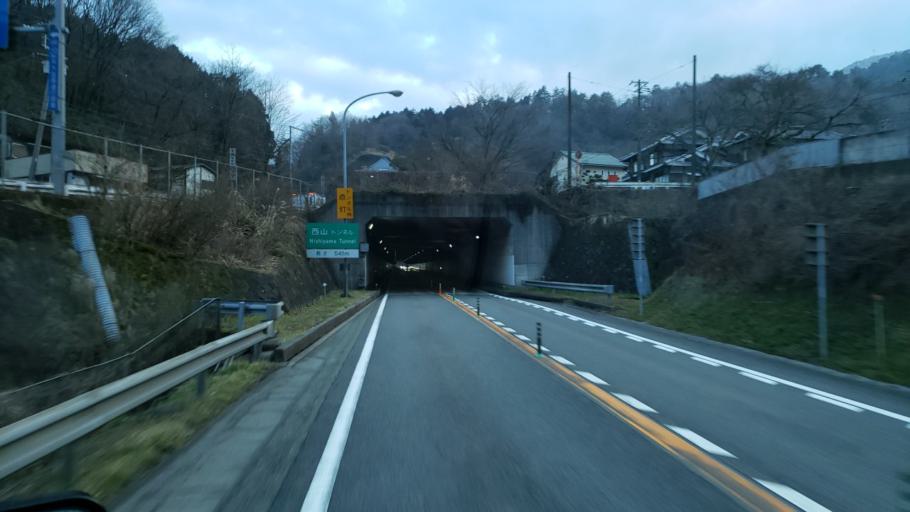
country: JP
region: Hyogo
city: Nishiwaki
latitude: 35.1725
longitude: 134.7915
